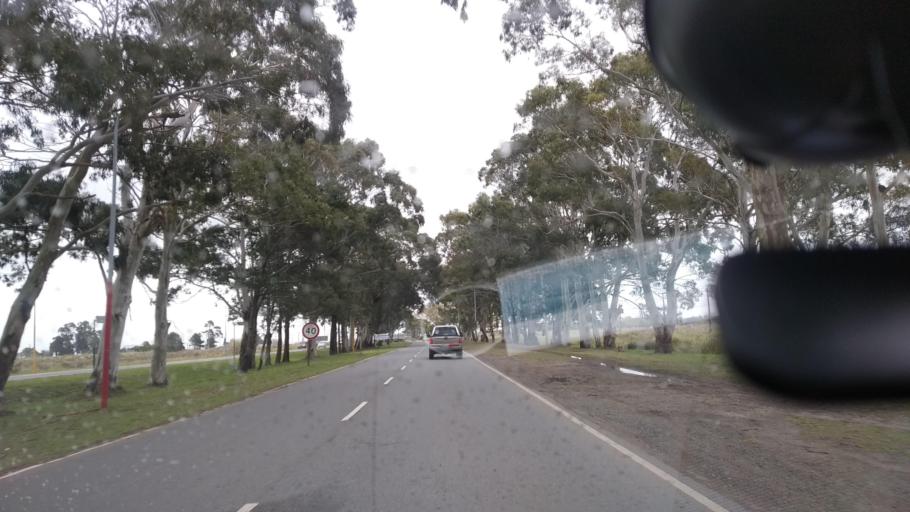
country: AR
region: Buenos Aires
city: San Clemente del Tuyu
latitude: -36.3869
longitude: -56.7317
